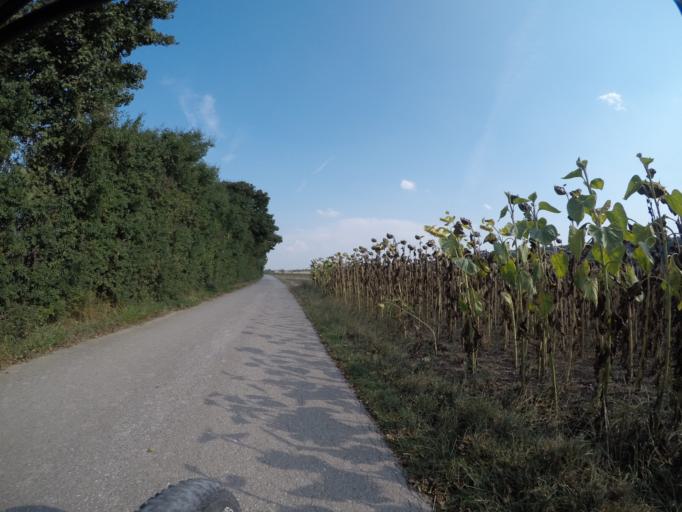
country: AT
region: Lower Austria
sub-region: Politischer Bezirk Baden
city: Hirtenberg
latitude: 47.9633
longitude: 16.1546
